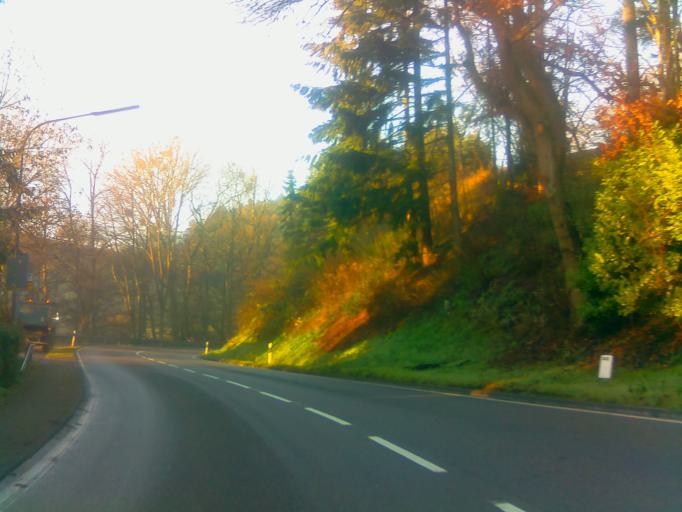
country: DE
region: Hesse
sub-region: Regierungsbezirk Darmstadt
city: Rimbach
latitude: 49.6455
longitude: 8.7214
